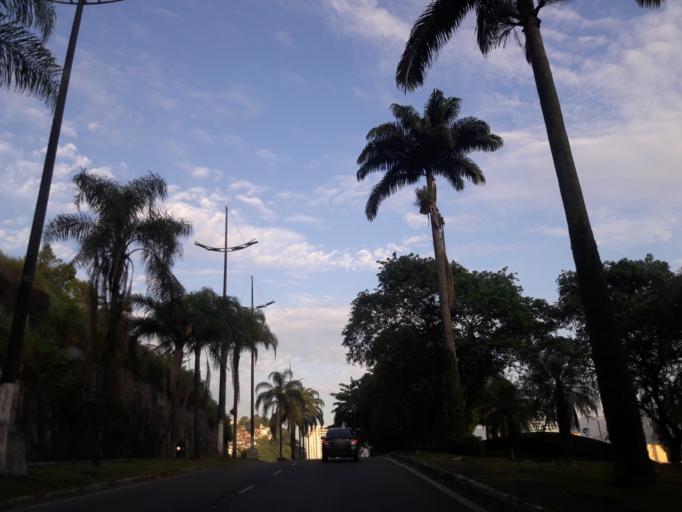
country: BR
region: Sao Paulo
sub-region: Santos
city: Santos
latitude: -23.9369
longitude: -46.3324
